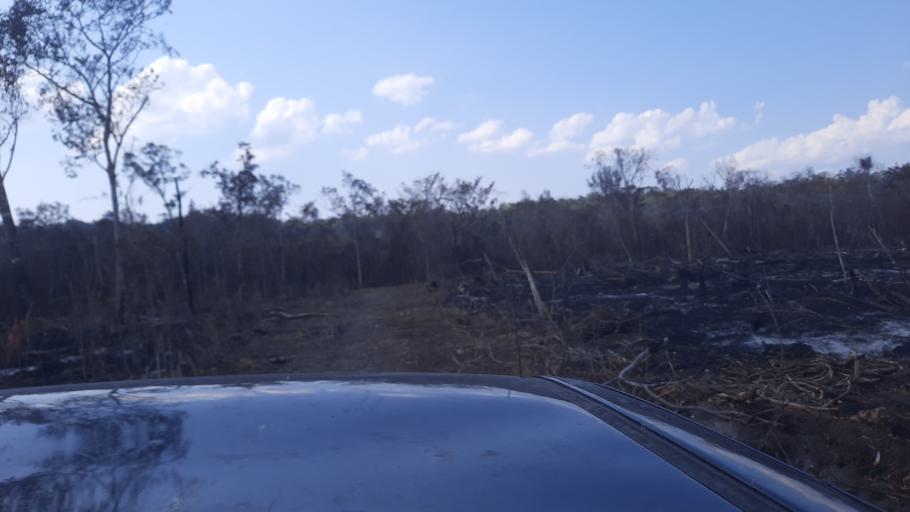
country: BZ
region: Cayo
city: Valley of Peace
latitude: 17.4050
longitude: -89.0366
